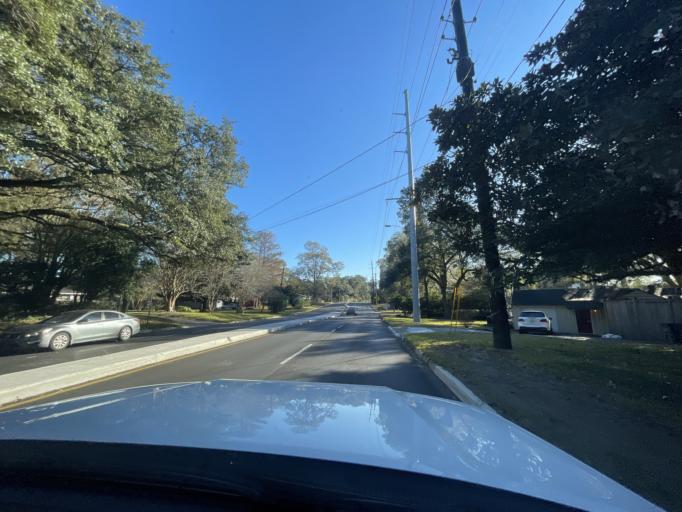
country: US
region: Louisiana
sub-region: East Baton Rouge Parish
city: Baton Rouge
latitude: 30.4338
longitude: -91.1527
